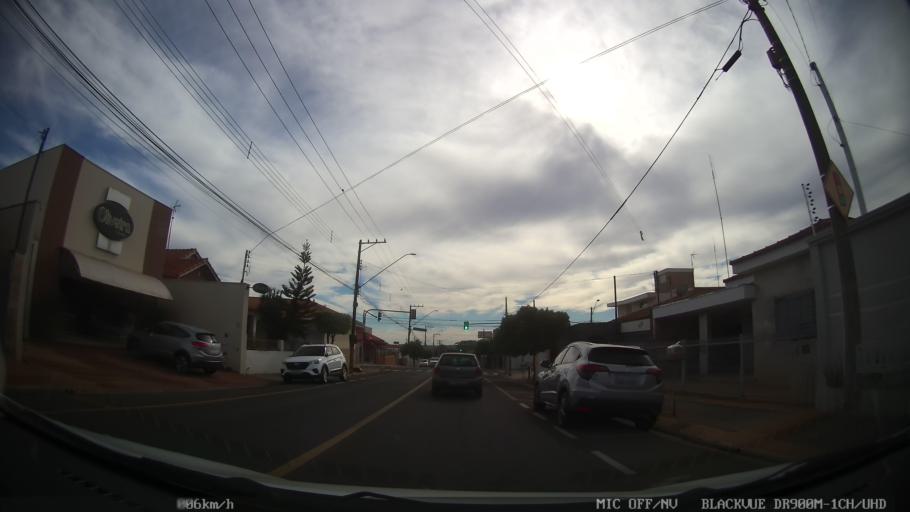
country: BR
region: Sao Paulo
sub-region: Catanduva
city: Catanduva
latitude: -21.1402
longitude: -48.9812
